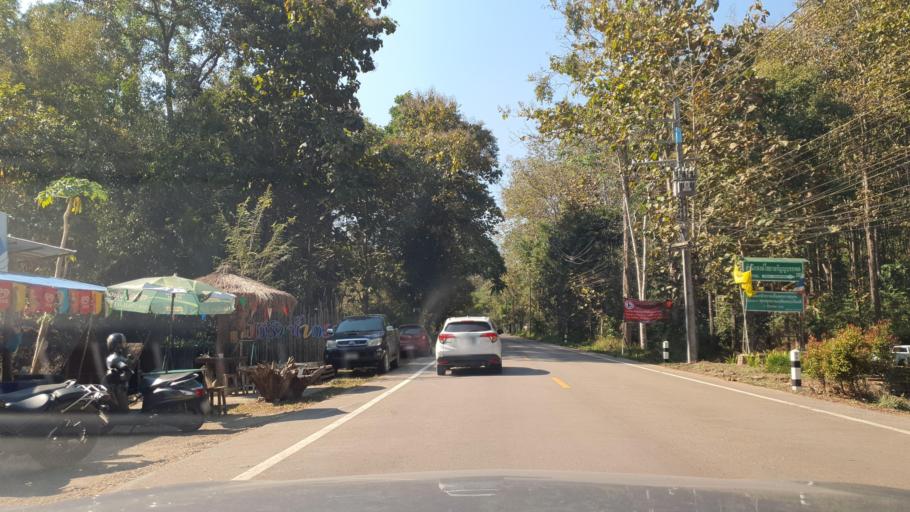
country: TH
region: Chiang Rai
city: Mae Lao
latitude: 19.8658
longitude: 99.6504
